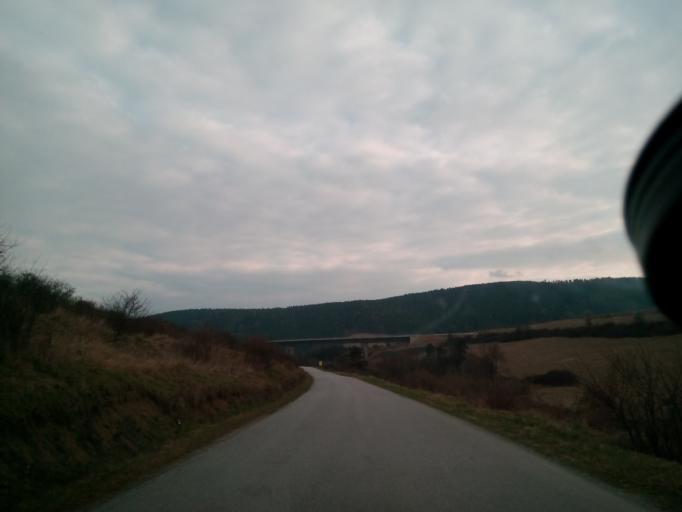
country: SK
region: Presovsky
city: Sabinov
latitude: 49.0323
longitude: 21.0188
